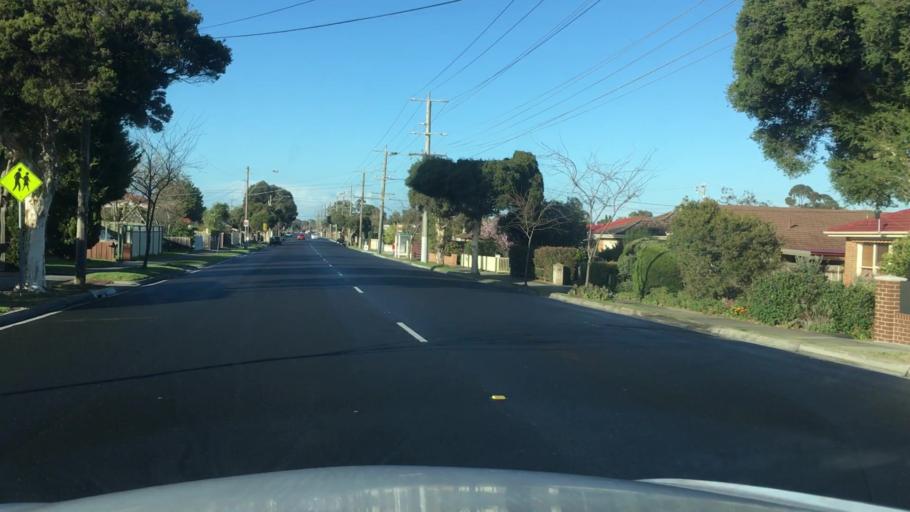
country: AU
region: Victoria
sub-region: Greater Dandenong
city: Keysborough
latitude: -37.9864
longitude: 145.1642
